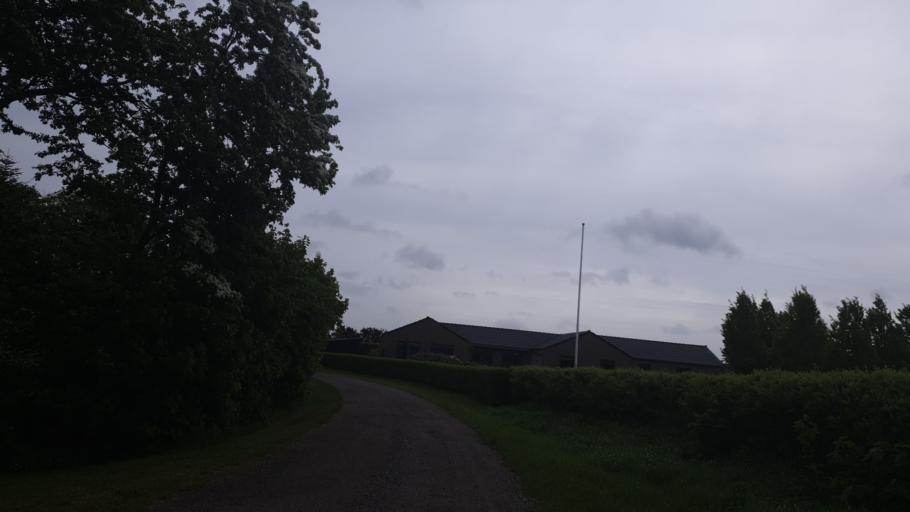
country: DK
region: Central Jutland
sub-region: Hedensted Kommune
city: Hedensted
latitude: 55.8135
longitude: 9.6980
